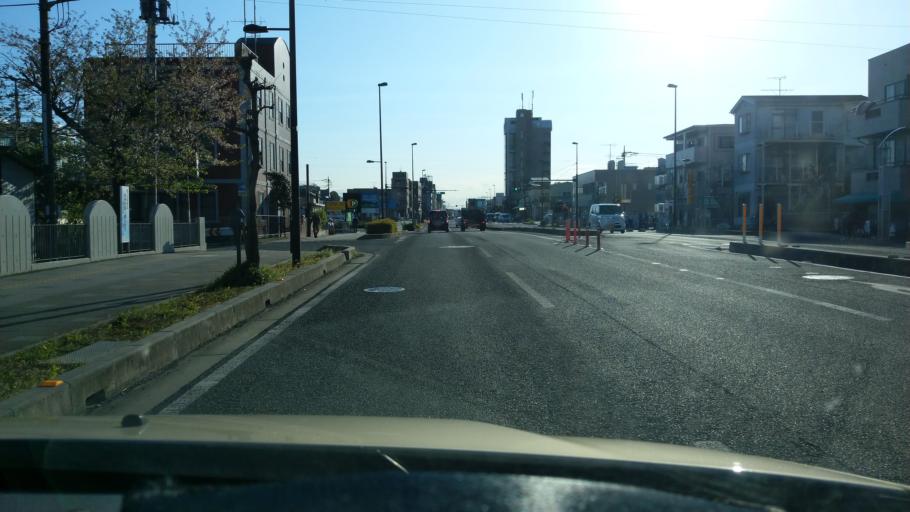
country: JP
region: Saitama
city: Yono
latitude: 35.9035
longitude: 139.6163
